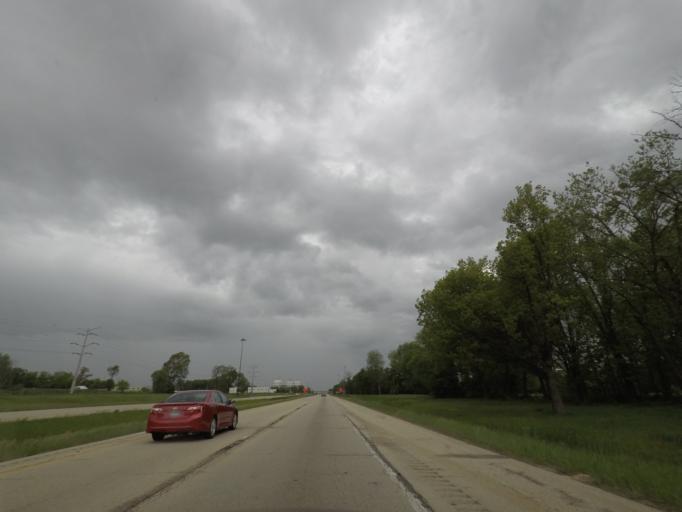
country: US
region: Illinois
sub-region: Winnebago County
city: Cherry Valley
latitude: 42.2203
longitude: -89.0155
